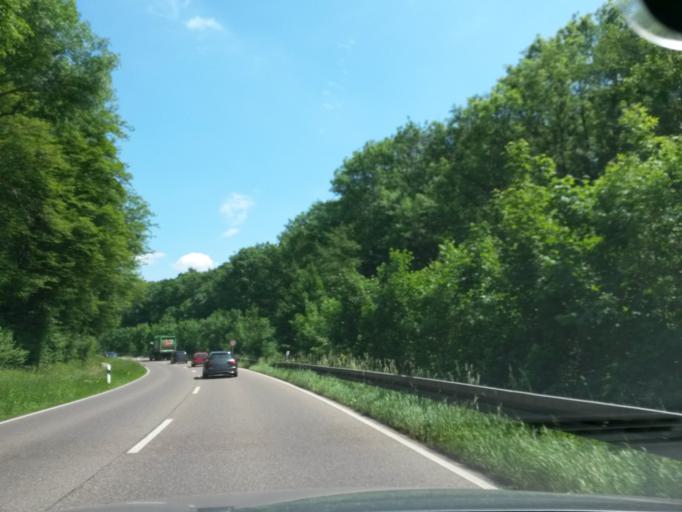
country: DE
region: Baden-Wuerttemberg
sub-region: Regierungsbezirk Stuttgart
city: Sersheim
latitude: 48.9640
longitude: 9.0427
